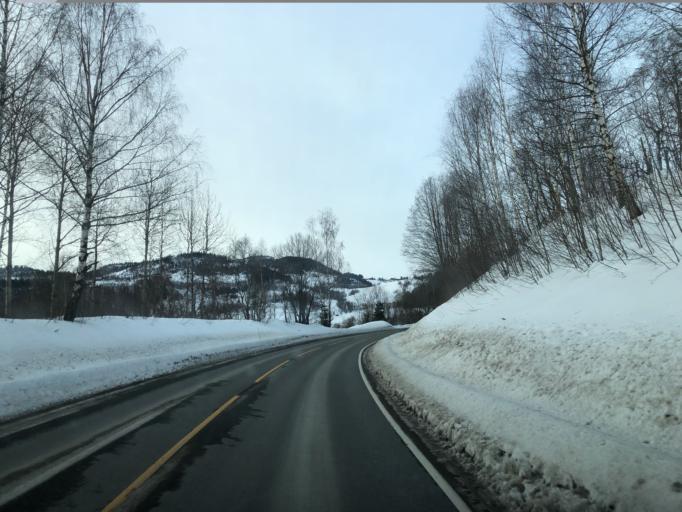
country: NO
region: Oppland
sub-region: Gausdal
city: Segalstad bru
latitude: 61.2699
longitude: 10.1460
